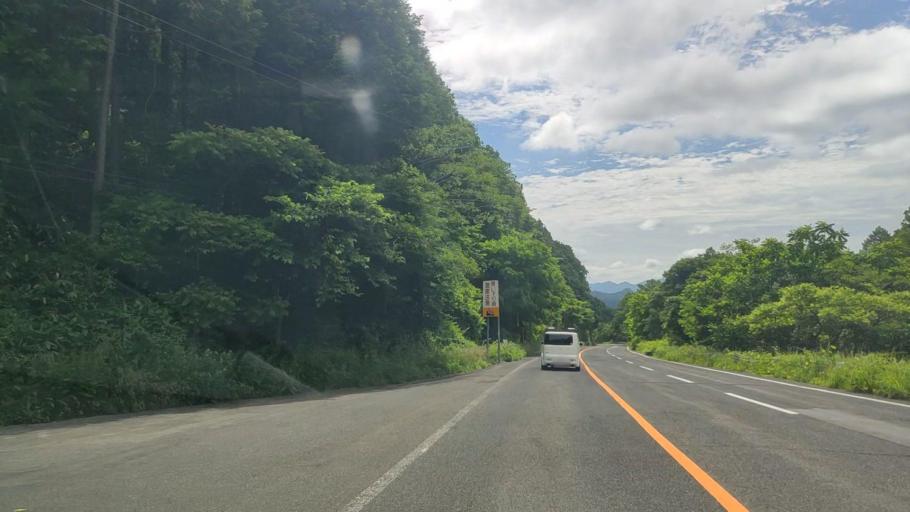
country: JP
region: Okayama
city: Niimi
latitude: 35.1831
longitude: 133.5371
